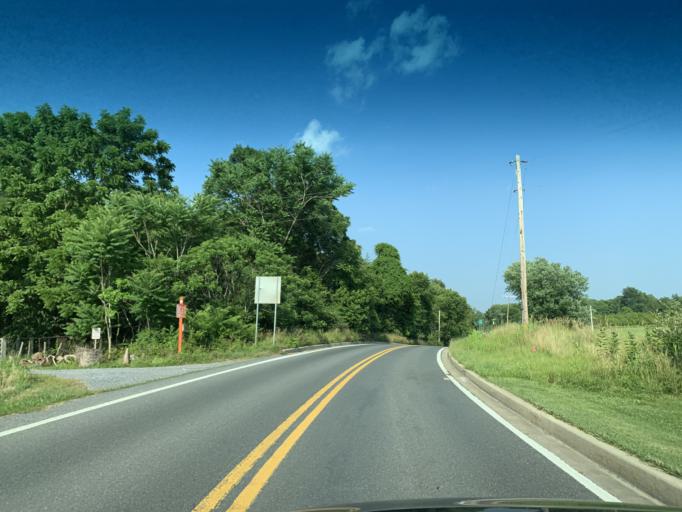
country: US
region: Maryland
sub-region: Frederick County
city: Green Valley
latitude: 39.2774
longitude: -77.3308
